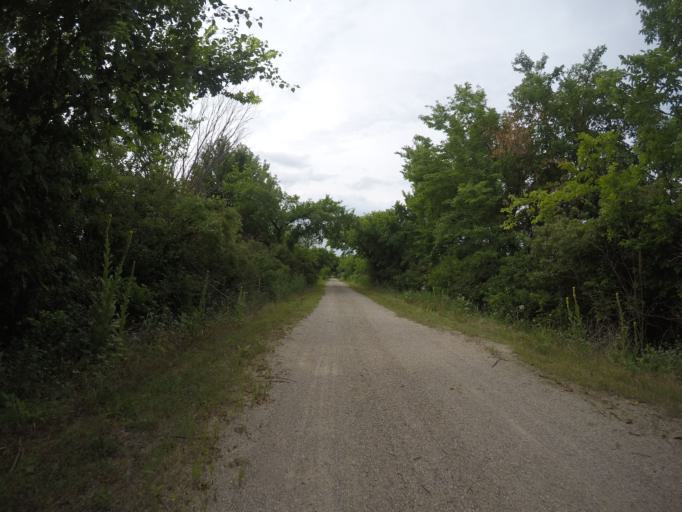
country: US
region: Kansas
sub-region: Franklin County
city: Ottawa
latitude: 38.5178
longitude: -95.2724
